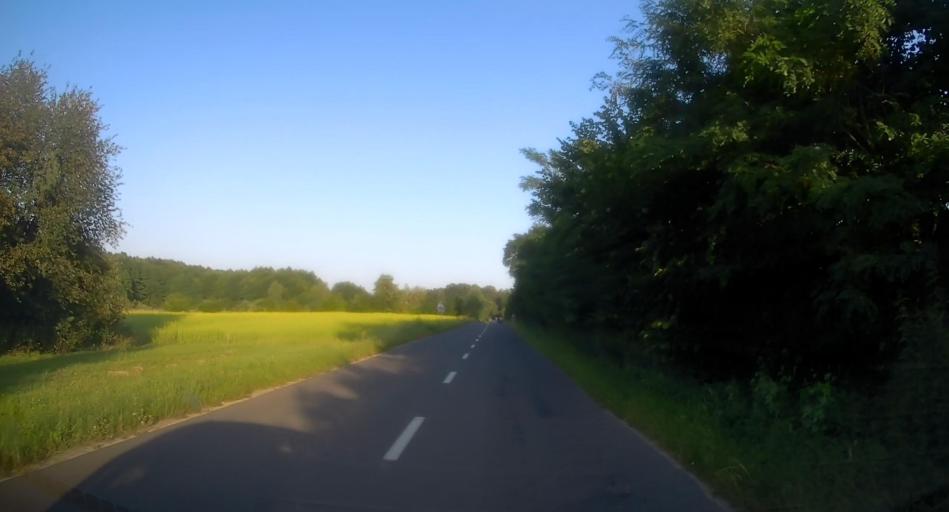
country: PL
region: Lodz Voivodeship
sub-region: Powiat skierniewicki
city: Kowiesy
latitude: 51.8942
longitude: 20.3824
